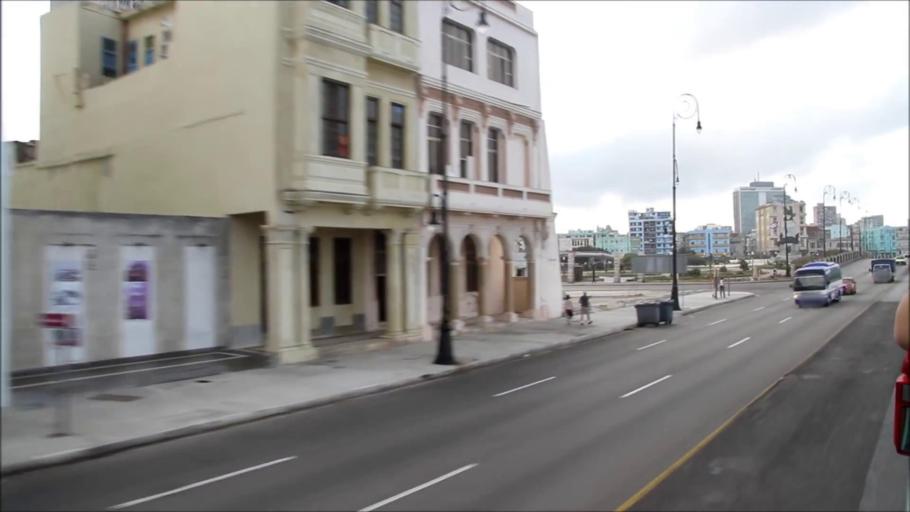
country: CU
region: La Habana
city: Centro Habana
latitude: 23.1416
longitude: -82.3701
